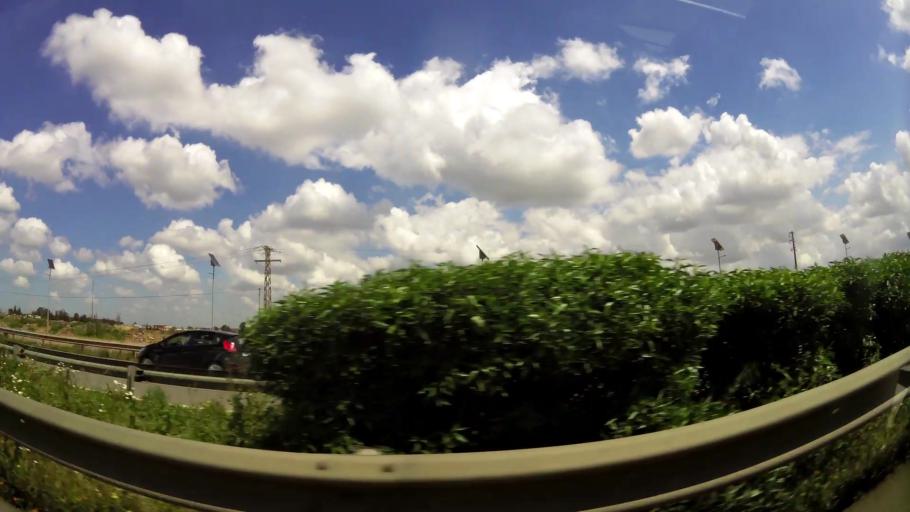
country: MA
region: Chaouia-Ouardigha
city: Nouaseur
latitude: 33.4143
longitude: -7.6265
